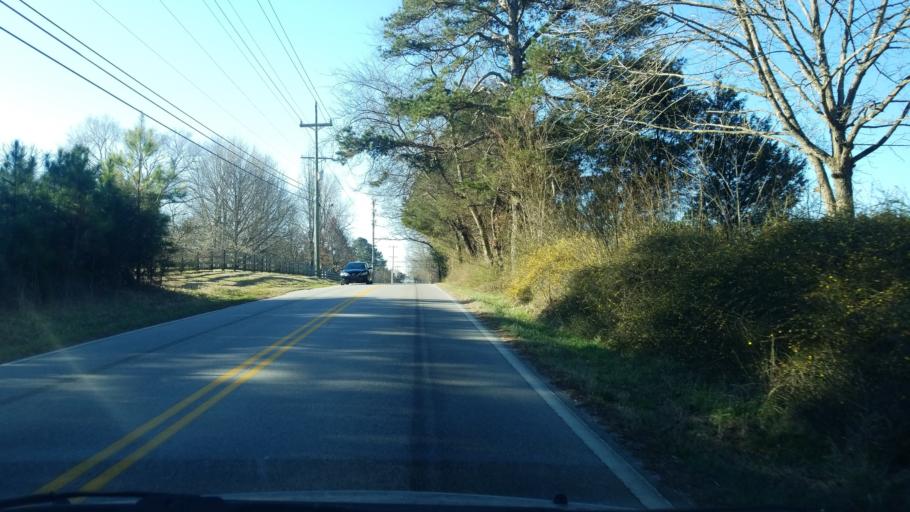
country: US
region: Tennessee
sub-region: Hamilton County
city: Collegedale
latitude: 35.0354
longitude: -85.0786
